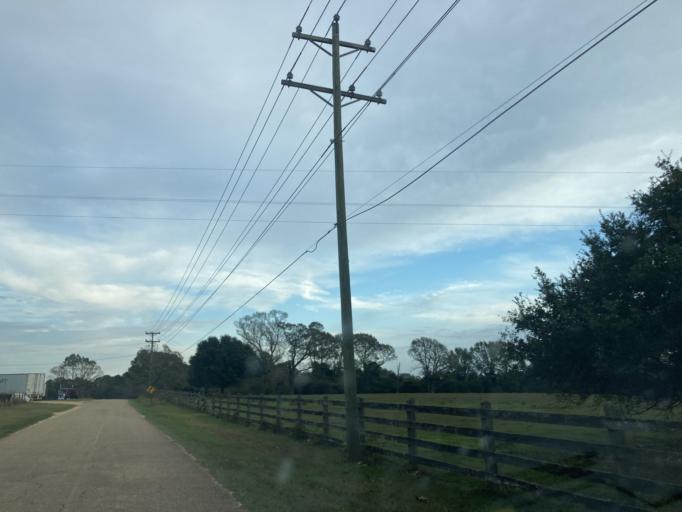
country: US
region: Mississippi
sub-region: Lamar County
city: Purvis
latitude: 31.1675
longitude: -89.3895
